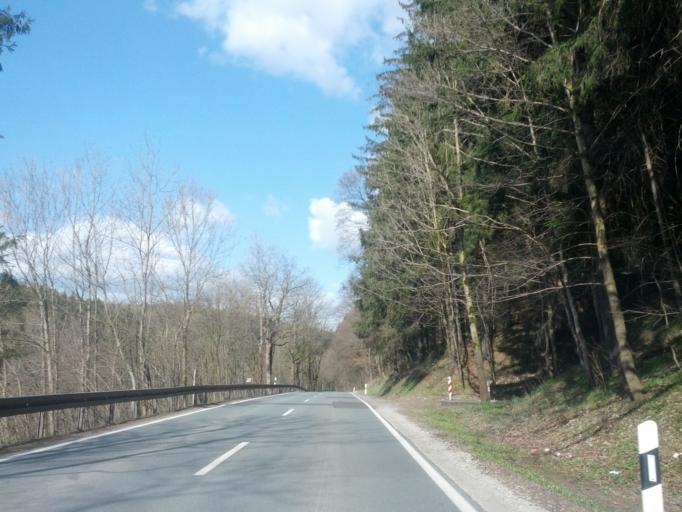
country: DE
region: Thuringia
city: Tambach-Dietharz
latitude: 50.8121
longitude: 10.6294
